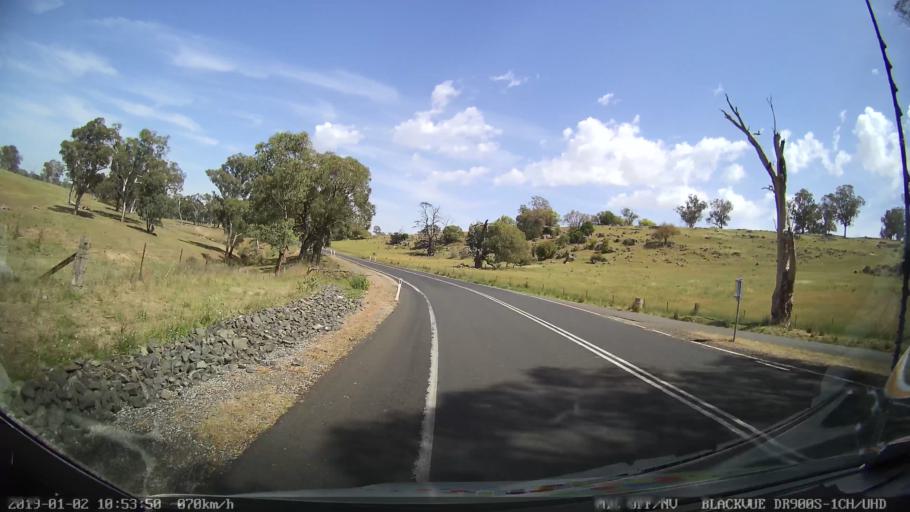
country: AU
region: New South Wales
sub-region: Cootamundra
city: Cootamundra
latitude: -34.6744
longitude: 148.2775
